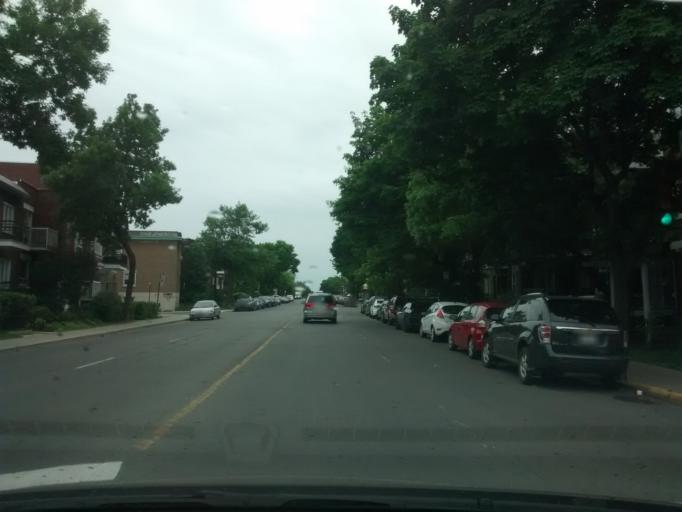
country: CA
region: Quebec
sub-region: Montreal
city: Saint-Leonard
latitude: 45.5501
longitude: -73.5833
